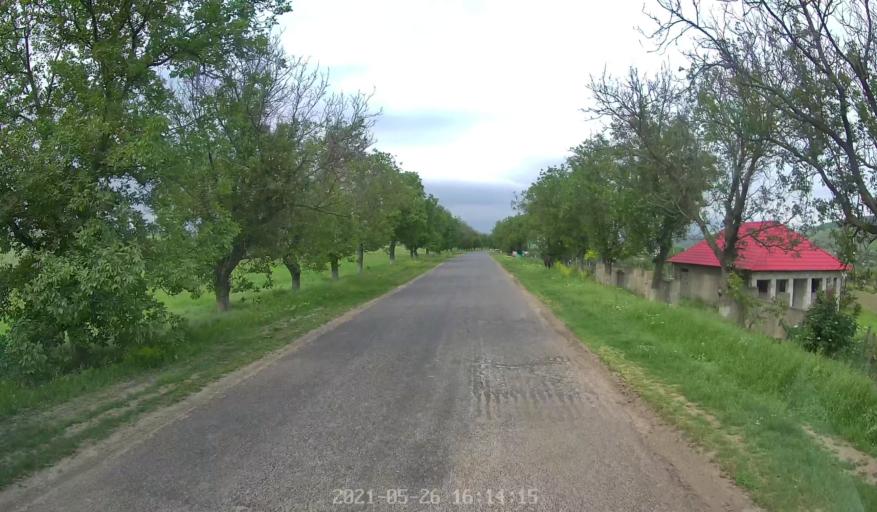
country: MD
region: Hincesti
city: Dancu
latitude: 46.7082
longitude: 28.3407
